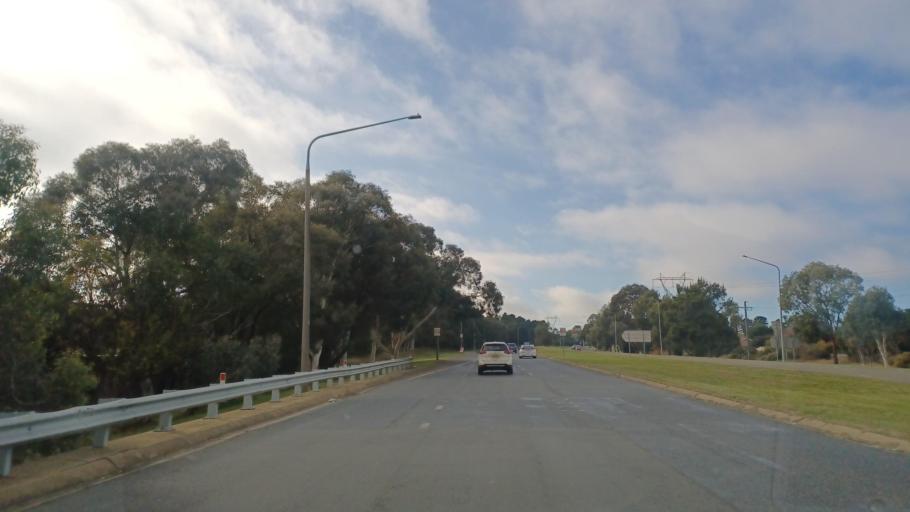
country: AU
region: Australian Capital Territory
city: Belconnen
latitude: -35.2198
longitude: 149.0548
